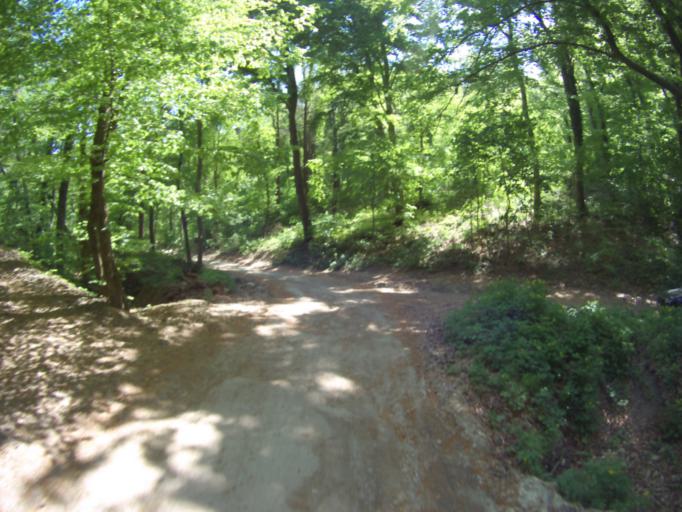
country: HU
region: Pest
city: Budaors
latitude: 47.4840
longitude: 18.9674
